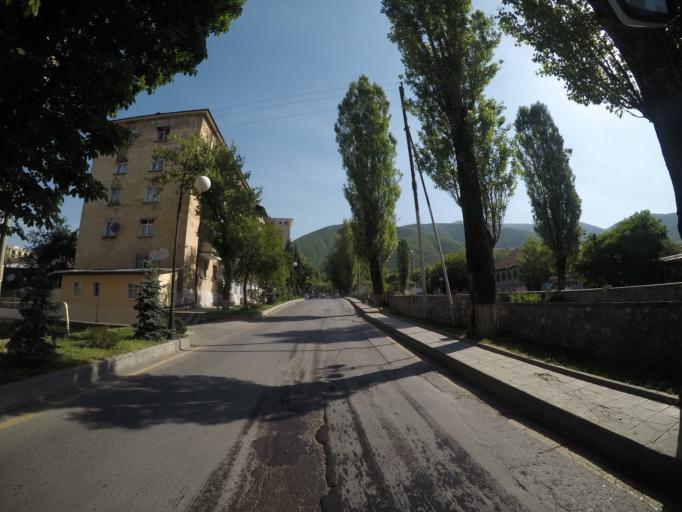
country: AZ
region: Shaki City
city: Sheki
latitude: 41.2012
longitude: 47.1796
